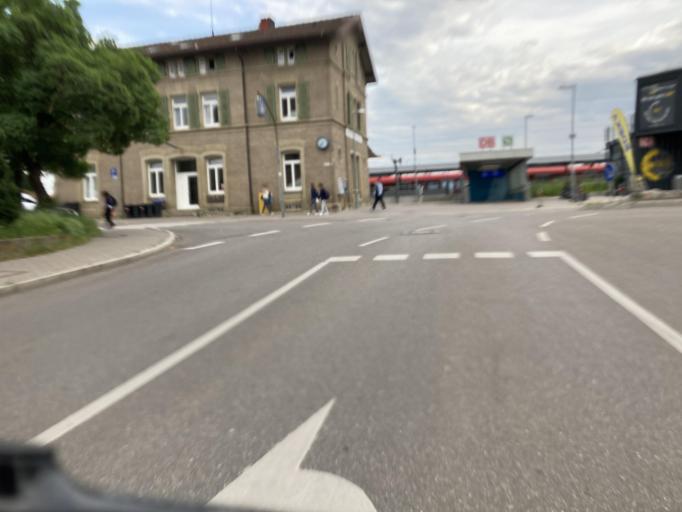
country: DE
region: Baden-Wuerttemberg
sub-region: Regierungsbezirk Stuttgart
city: Renningen
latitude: 48.7746
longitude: 8.9328
